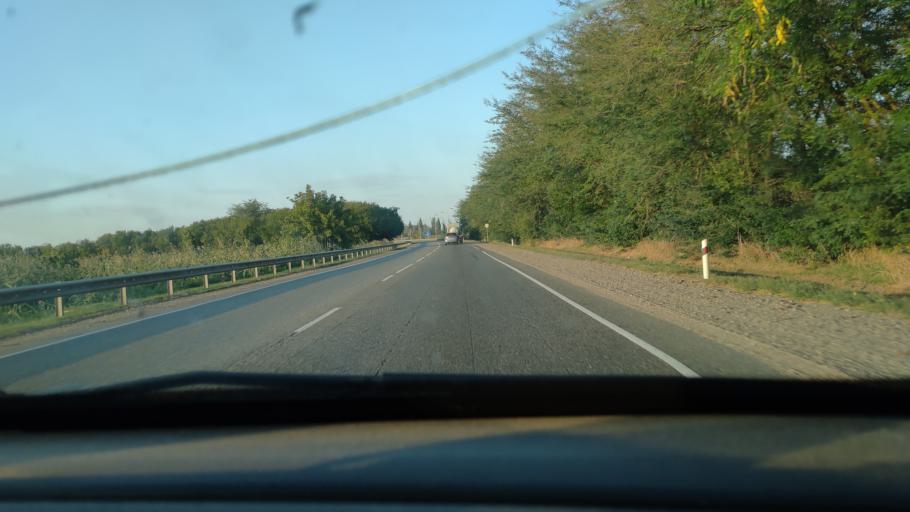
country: RU
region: Krasnodarskiy
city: Kanevskaya
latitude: 46.0694
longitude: 39.0115
